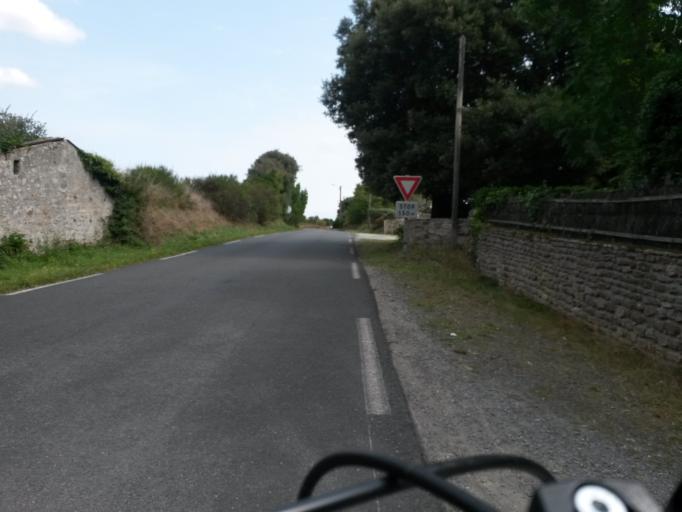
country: FR
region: Pays de la Loire
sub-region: Departement de la Loire-Atlantique
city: Guerande
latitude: 47.3293
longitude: -2.4513
